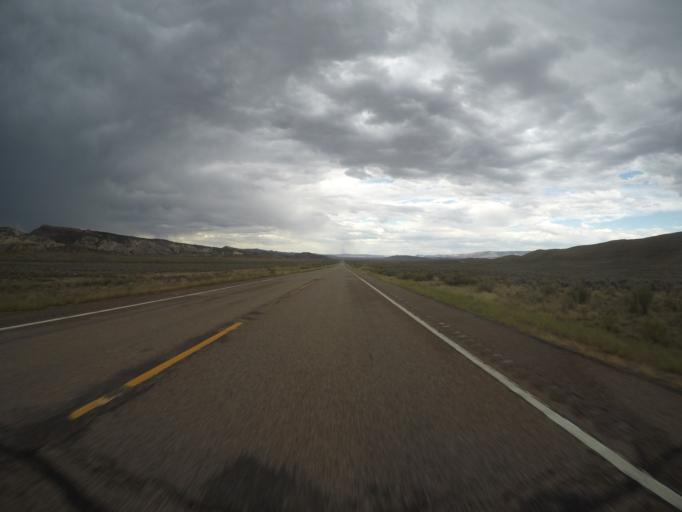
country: US
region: Colorado
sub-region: Rio Blanco County
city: Rangely
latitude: 40.2511
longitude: -108.7901
